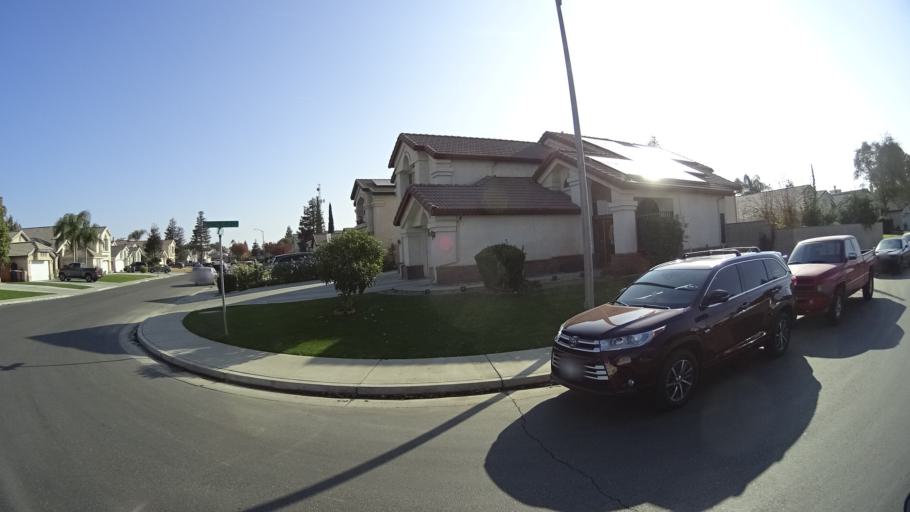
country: US
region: California
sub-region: Kern County
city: Greenacres
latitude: 35.3665
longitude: -119.1155
